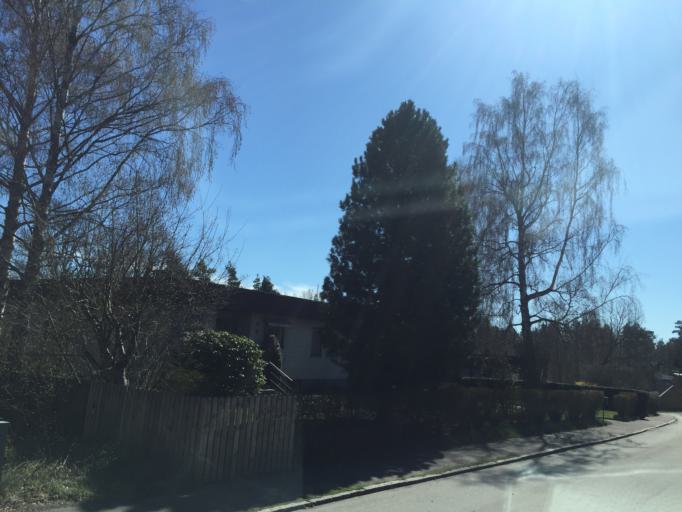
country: SE
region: Kalmar
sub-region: Oskarshamns Kommun
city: Oskarshamn
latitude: 57.2565
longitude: 16.4507
